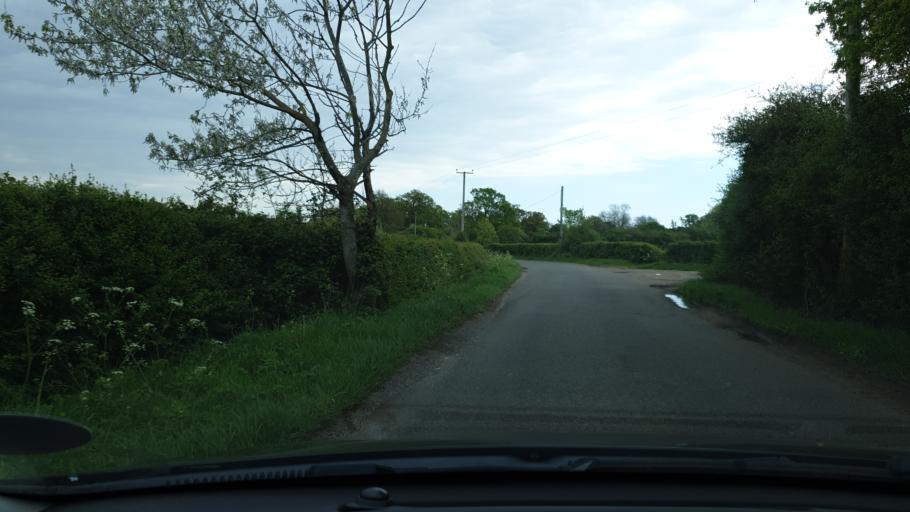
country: GB
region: England
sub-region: Essex
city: Great Bentley
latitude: 51.8898
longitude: 1.0688
